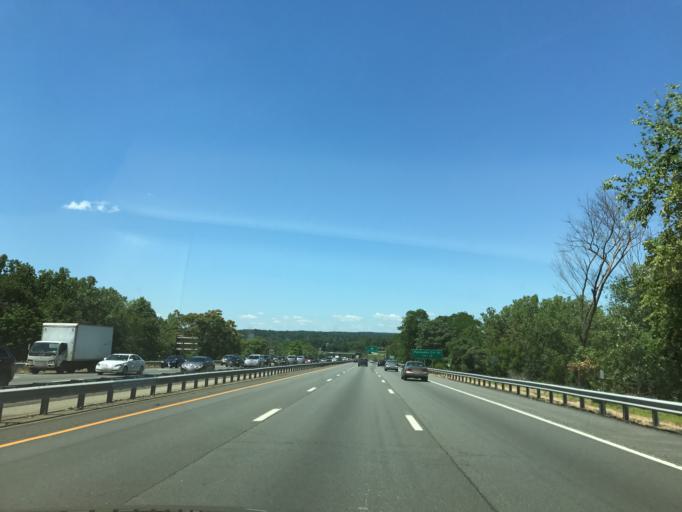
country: US
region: New York
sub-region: Rockland County
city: Valley Cottage
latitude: 41.0983
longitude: -73.9456
